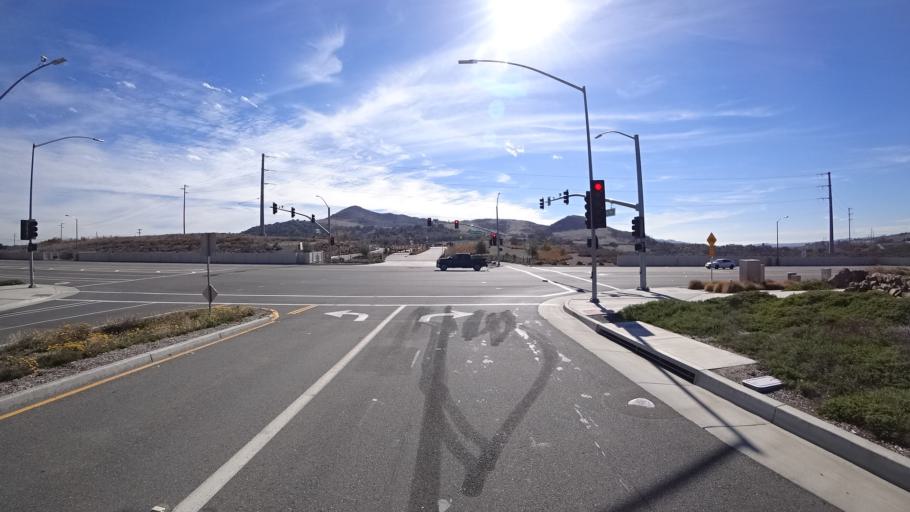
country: US
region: California
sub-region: Orange County
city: Ladera Ranch
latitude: 33.5295
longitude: -117.6059
